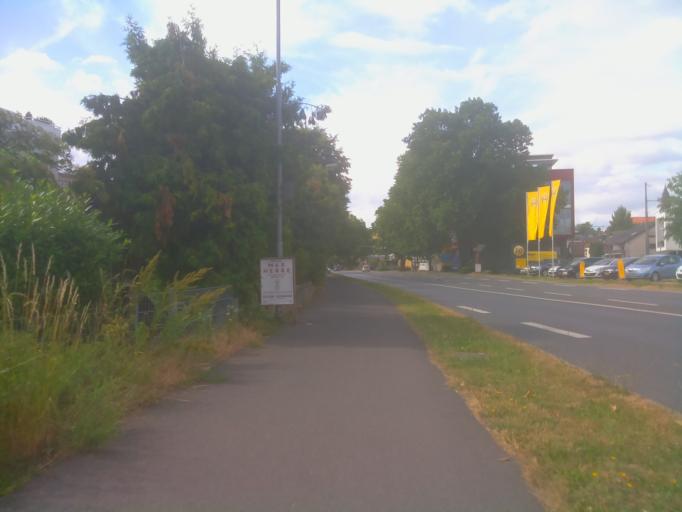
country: DE
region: Baden-Wuerttemberg
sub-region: Karlsruhe Region
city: Dossenheim
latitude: 49.4440
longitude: 8.6760
